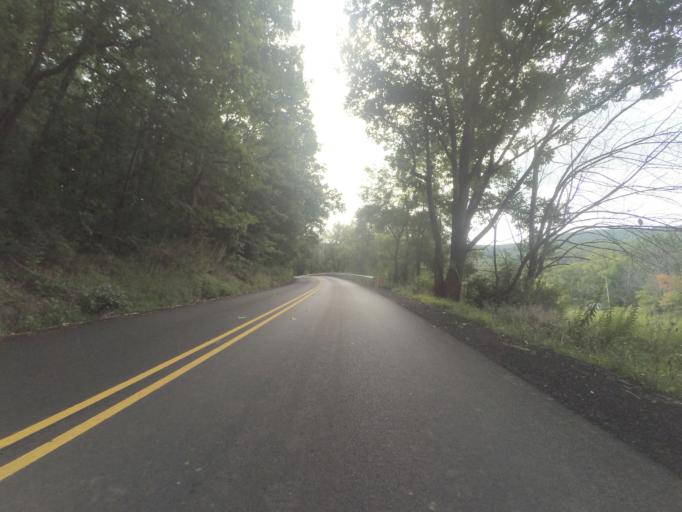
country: US
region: Pennsylvania
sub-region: Centre County
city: Milesburg
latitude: 40.9994
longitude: -77.8071
